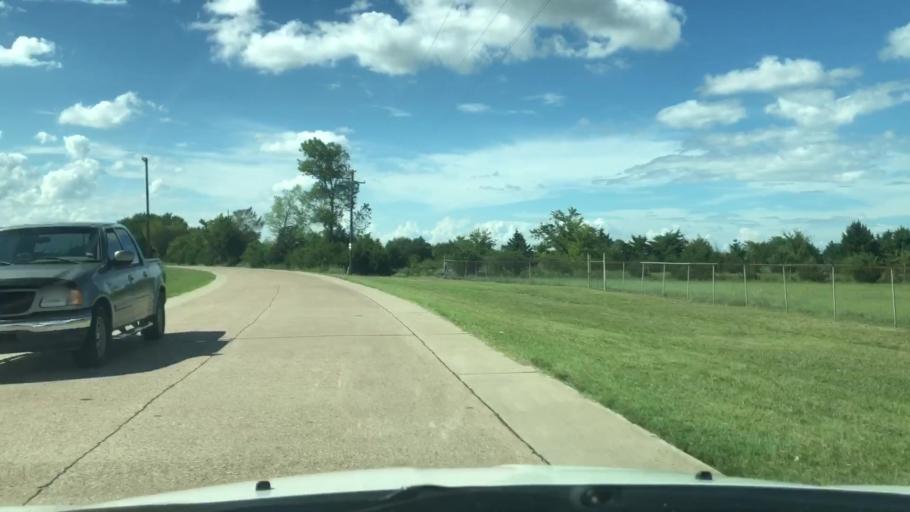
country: US
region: Texas
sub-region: Navarro County
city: Corsicana
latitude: 32.0316
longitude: -96.3964
